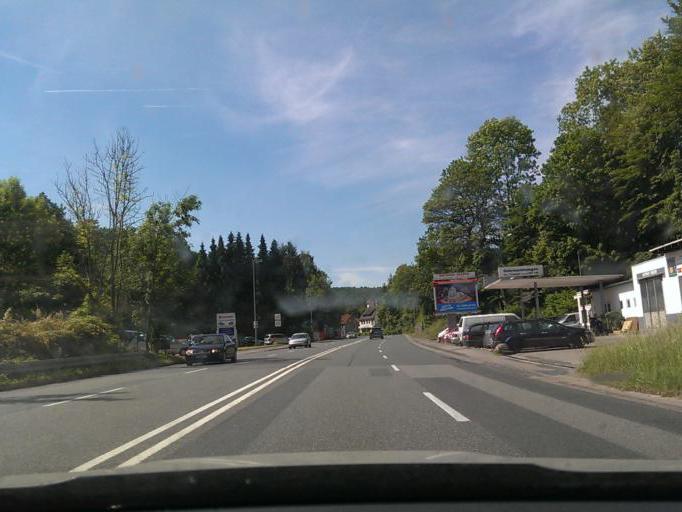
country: DE
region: Lower Saxony
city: Alfeld
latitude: 51.9723
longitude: 9.8094
